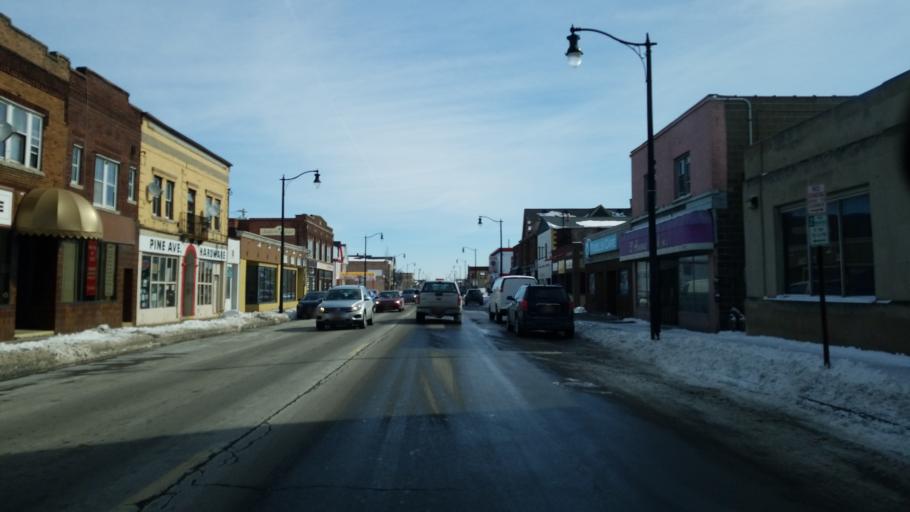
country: US
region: New York
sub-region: Niagara County
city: Niagara Falls
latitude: 43.0951
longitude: -79.0389
